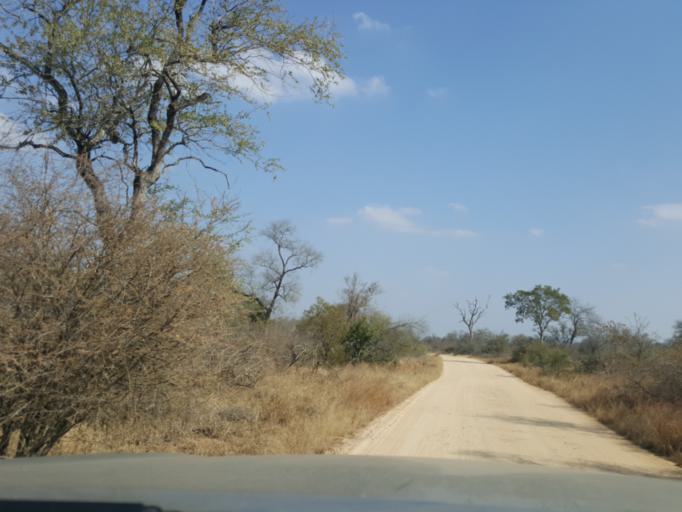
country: ZA
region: Mpumalanga
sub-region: Ehlanzeni District
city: Komatipoort
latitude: -25.2782
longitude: 31.7772
